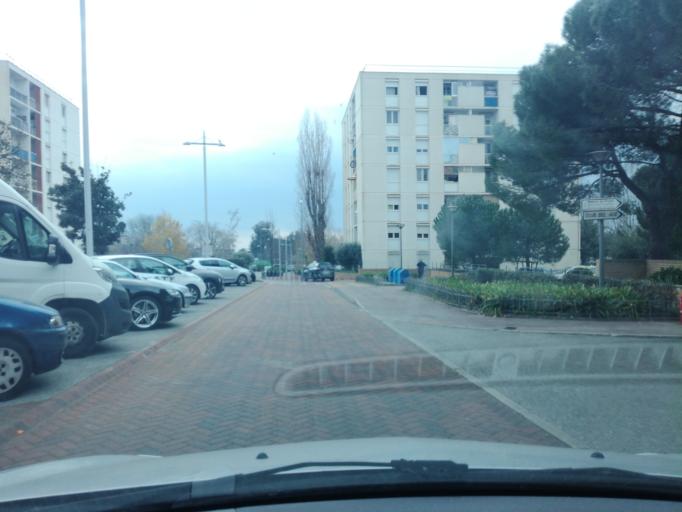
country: FR
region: Provence-Alpes-Cote d'Azur
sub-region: Departement des Alpes-Maritimes
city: Mandelieu-la-Napoule
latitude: 43.5569
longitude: 6.9629
